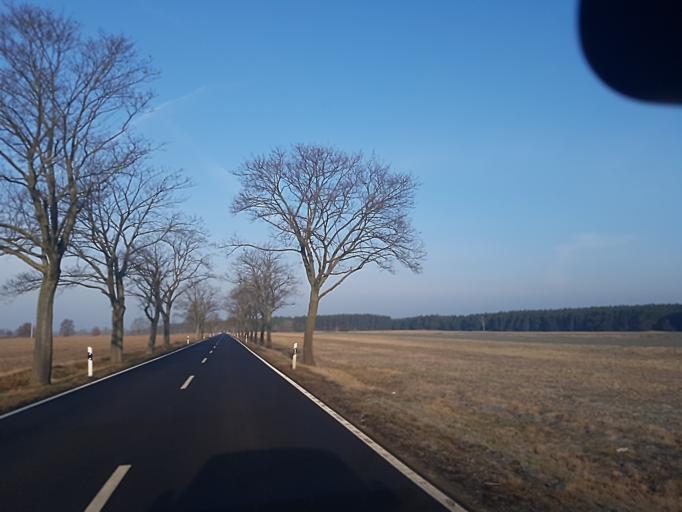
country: DE
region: Brandenburg
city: Golzow
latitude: 52.2656
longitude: 12.6526
